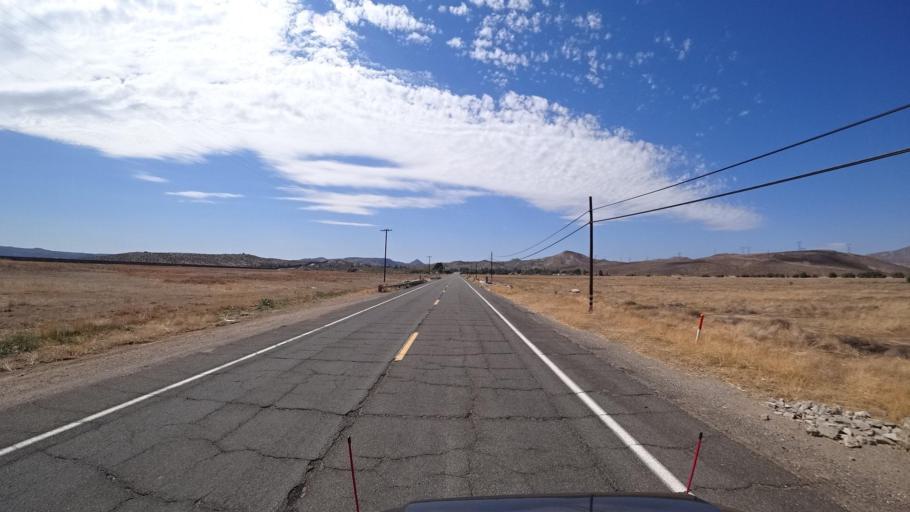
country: MX
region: Baja California
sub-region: Tecate
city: Cereso del Hongo
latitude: 32.6176
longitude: -116.1726
